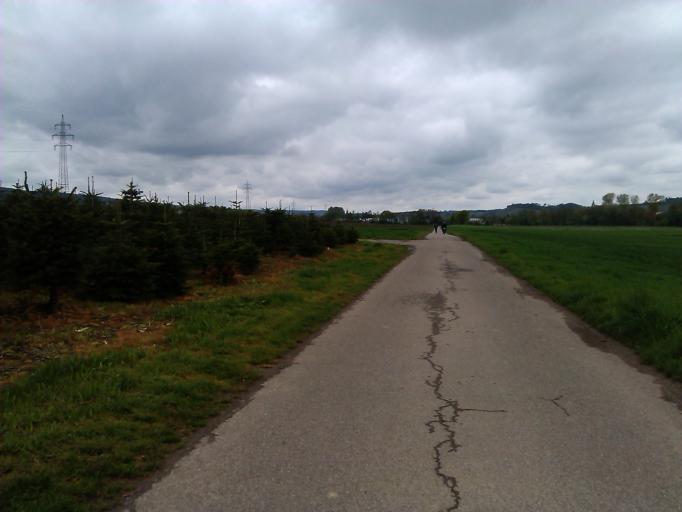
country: DE
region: Baden-Wuerttemberg
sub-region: Regierungsbezirk Stuttgart
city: Guglingen
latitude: 49.0630
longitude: 9.0204
